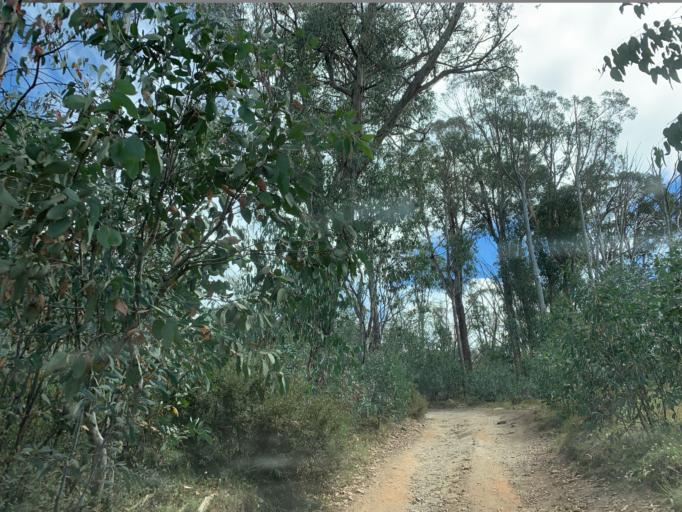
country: AU
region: Victoria
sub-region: Mansfield
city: Mansfield
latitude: -37.1027
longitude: 146.5408
